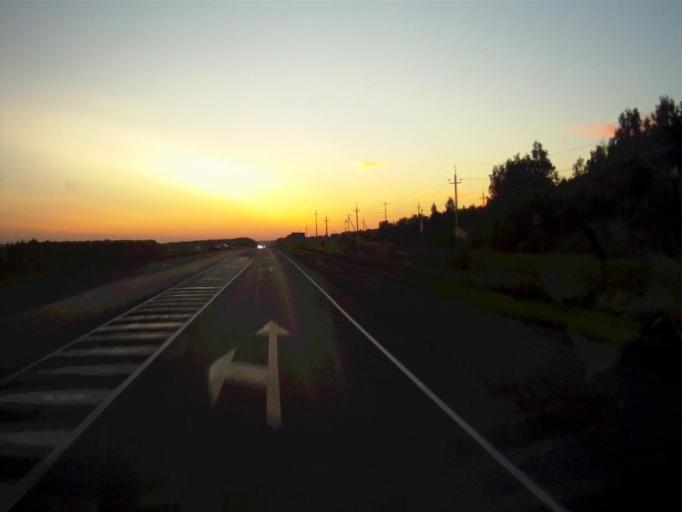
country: RU
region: Chelyabinsk
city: Poletayevo
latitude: 55.2143
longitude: 61.0597
